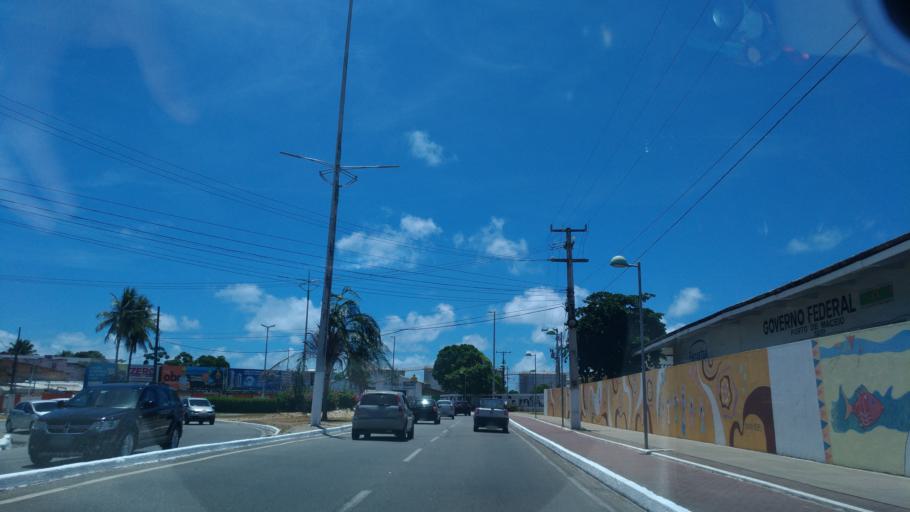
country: BR
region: Alagoas
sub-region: Maceio
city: Maceio
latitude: -9.6740
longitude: -35.7205
